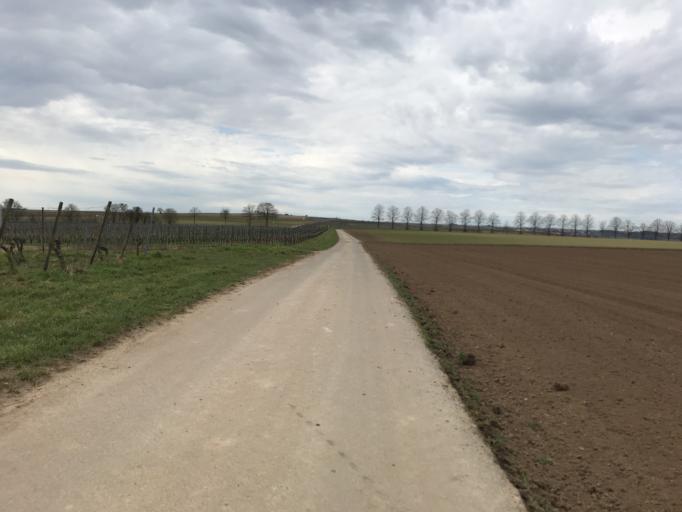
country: DE
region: Rheinland-Pfalz
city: Ober-Saulheim
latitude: 49.8866
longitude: 8.1389
